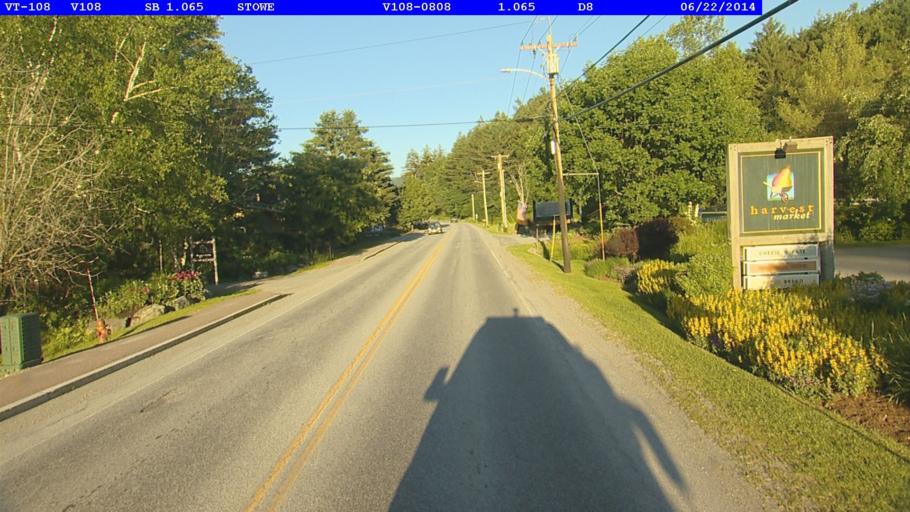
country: US
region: Vermont
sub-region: Lamoille County
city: Morristown
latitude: 44.4740
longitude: -72.6990
